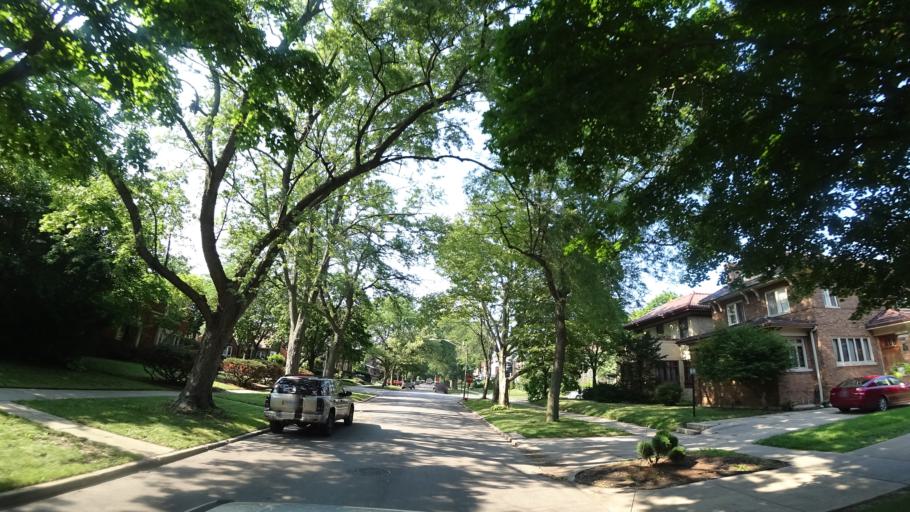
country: US
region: Illinois
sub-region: Cook County
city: Chicago
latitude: 41.7711
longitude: -87.5813
